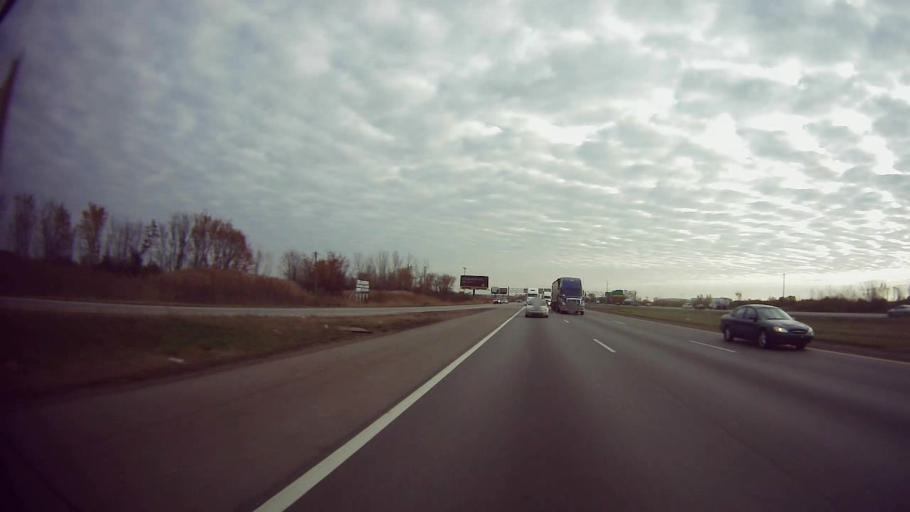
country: US
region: Michigan
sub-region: Wayne County
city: Romulus
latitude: 42.2339
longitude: -83.3635
